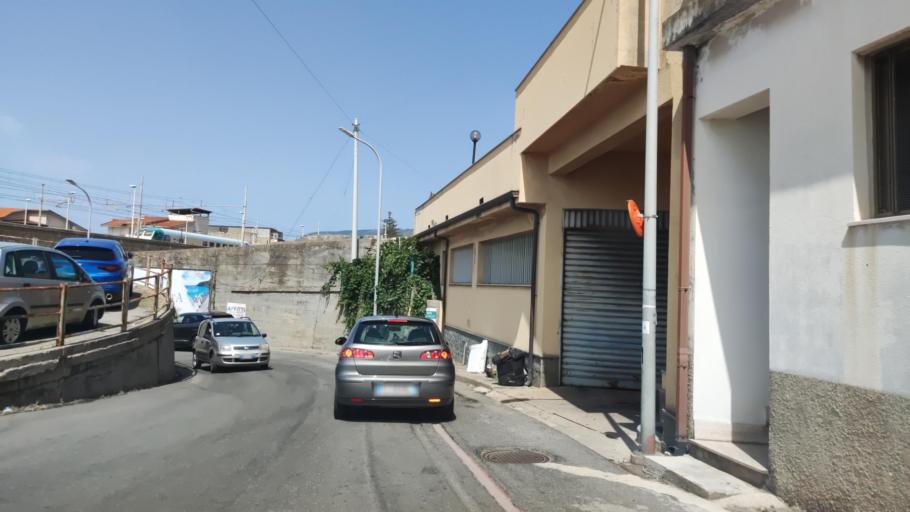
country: IT
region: Calabria
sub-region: Provincia di Reggio Calabria
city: Bagnara Calabra
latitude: 38.2815
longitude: 15.7994
